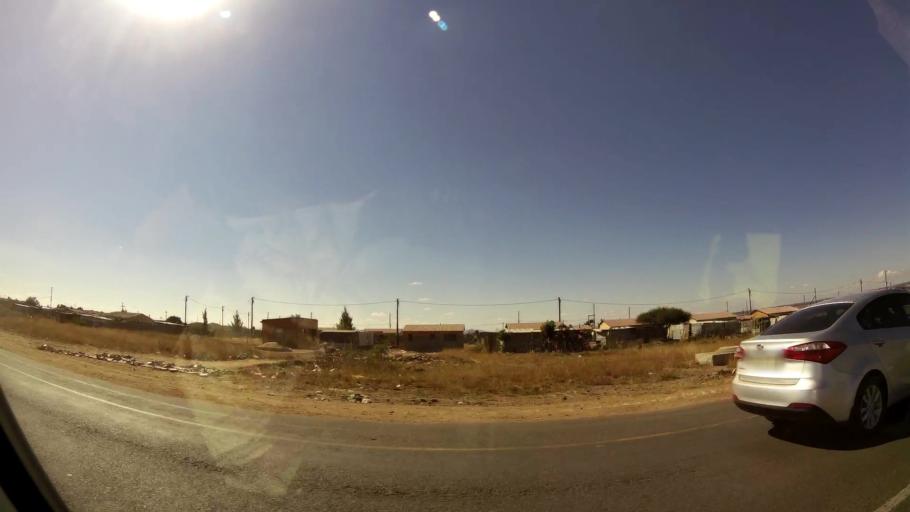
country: ZA
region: Limpopo
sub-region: Capricorn District Municipality
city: Polokwane
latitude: -23.8618
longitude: 29.4147
